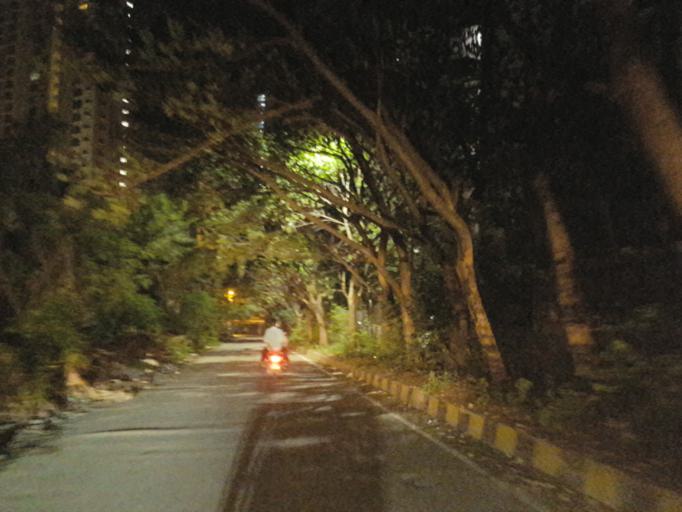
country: IN
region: Telangana
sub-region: Rangareddi
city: Kukatpalli
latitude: 17.4766
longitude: 78.3932
